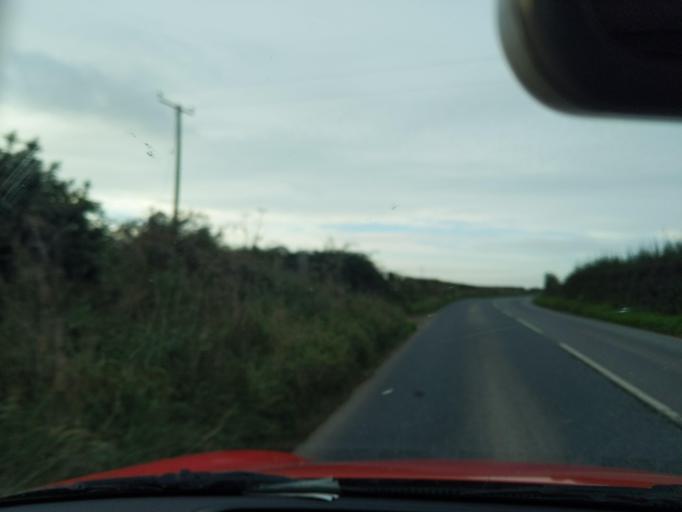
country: GB
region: England
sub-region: Devon
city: Great Torrington
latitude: 50.9145
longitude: -4.1409
